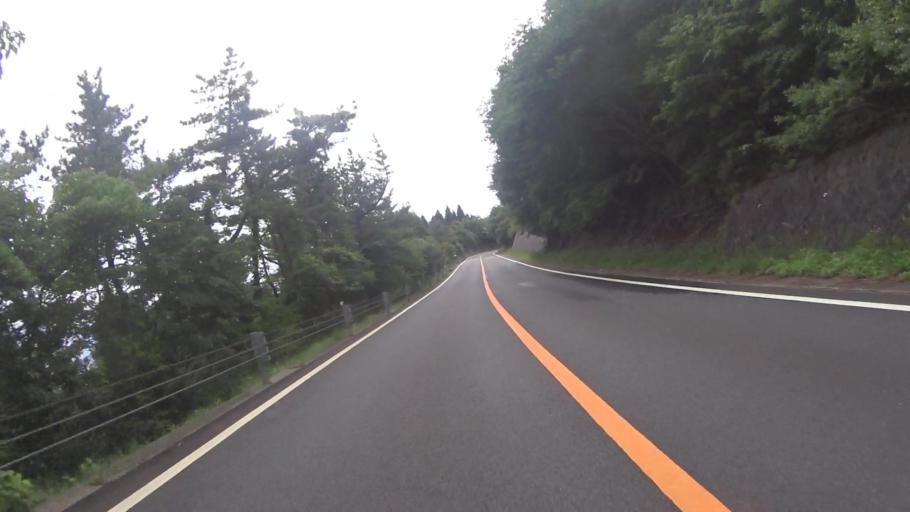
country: JP
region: Oita
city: Tsukawaki
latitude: 33.0895
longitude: 131.1974
